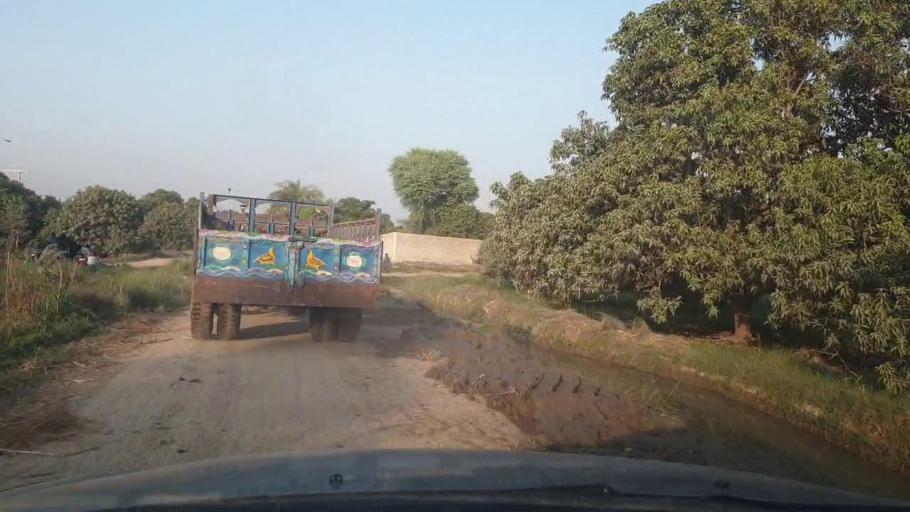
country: PK
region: Sindh
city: Tando Jam
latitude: 25.4234
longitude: 68.4940
